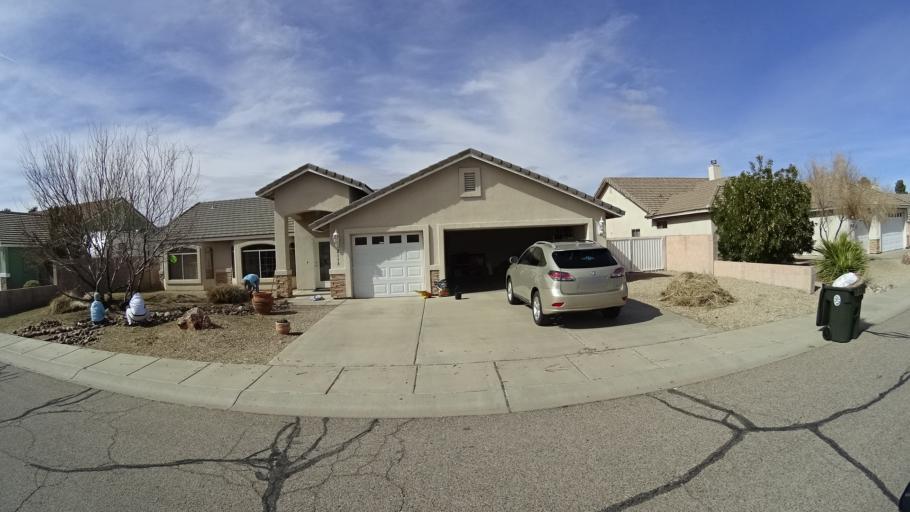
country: US
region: Arizona
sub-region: Mohave County
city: New Kingman-Butler
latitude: 35.2332
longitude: -114.0289
